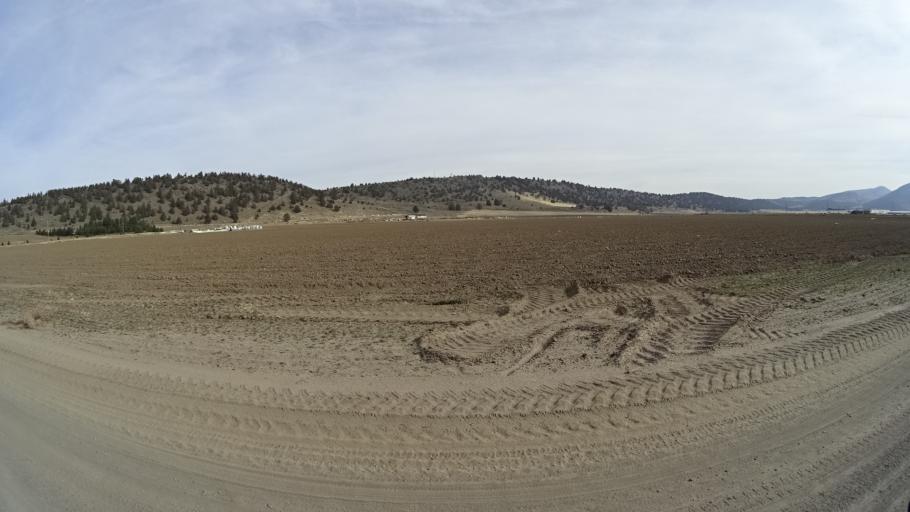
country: US
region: Oregon
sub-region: Klamath County
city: Klamath Falls
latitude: 41.9644
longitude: -121.9113
